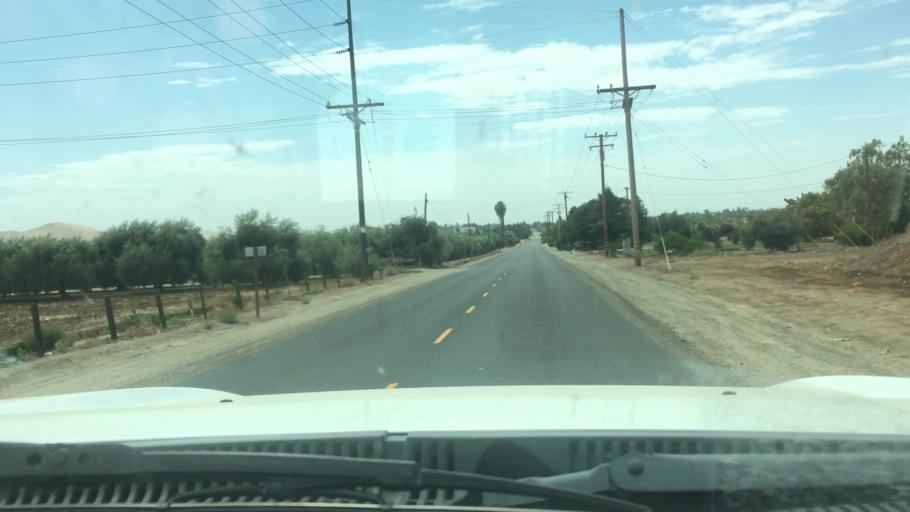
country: US
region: California
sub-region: Tulare County
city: Porterville
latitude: 36.0955
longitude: -119.0088
